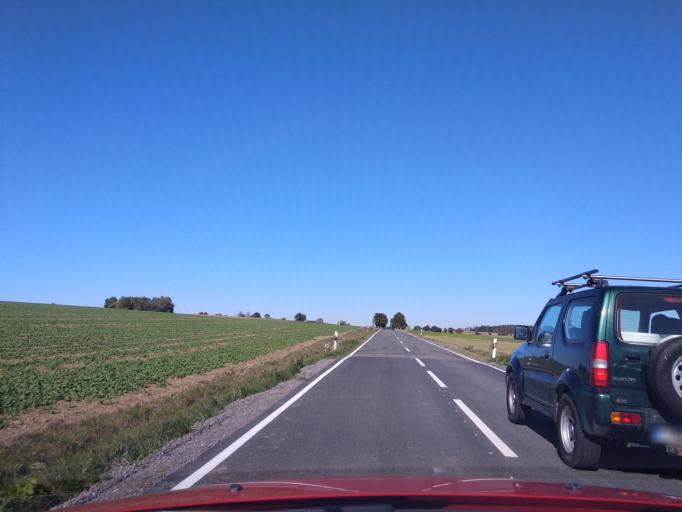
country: DE
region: Lower Saxony
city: Boffzen
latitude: 51.7331
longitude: 9.2976
